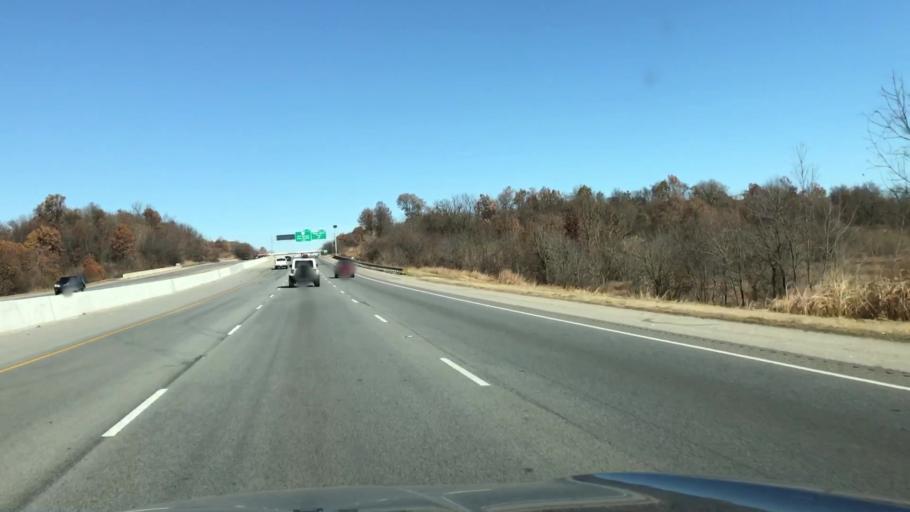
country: US
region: Arkansas
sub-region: Benton County
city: Bethel Heights
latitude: 36.2187
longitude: -94.1810
